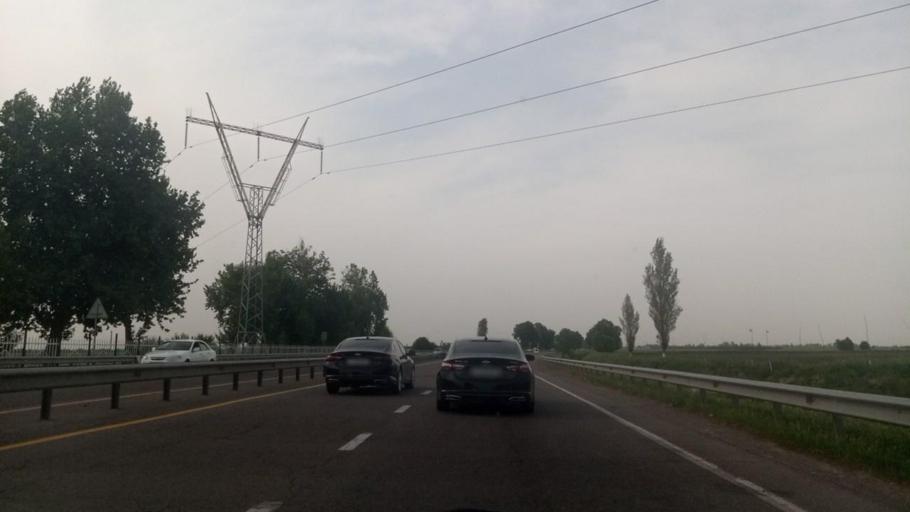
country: UZ
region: Toshkent Shahri
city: Bektemir
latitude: 41.1869
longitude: 69.4037
